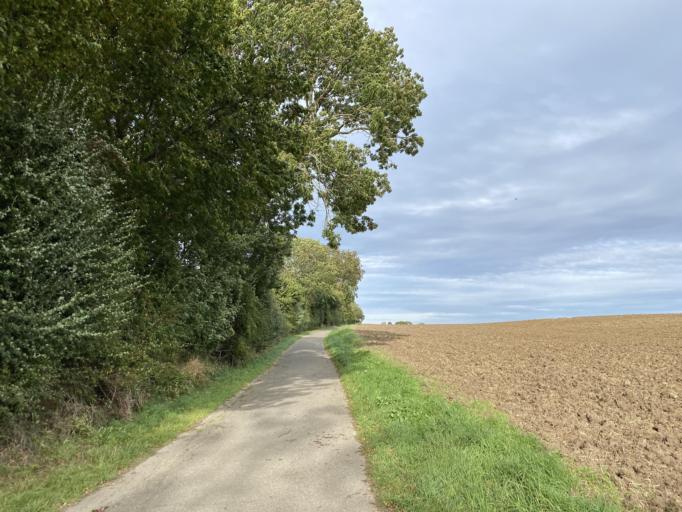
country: DE
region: Schleswig-Holstein
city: Grube
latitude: 54.2608
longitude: 11.0468
